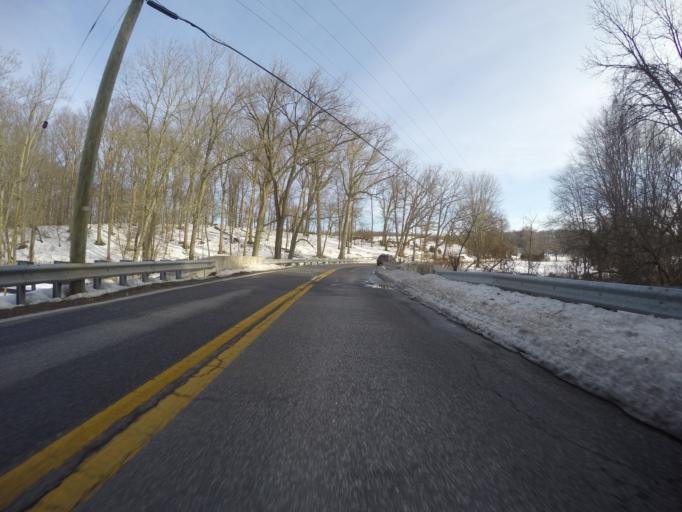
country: US
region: Maryland
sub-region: Harford County
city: Jarrettsville
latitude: 39.5389
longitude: -76.5482
